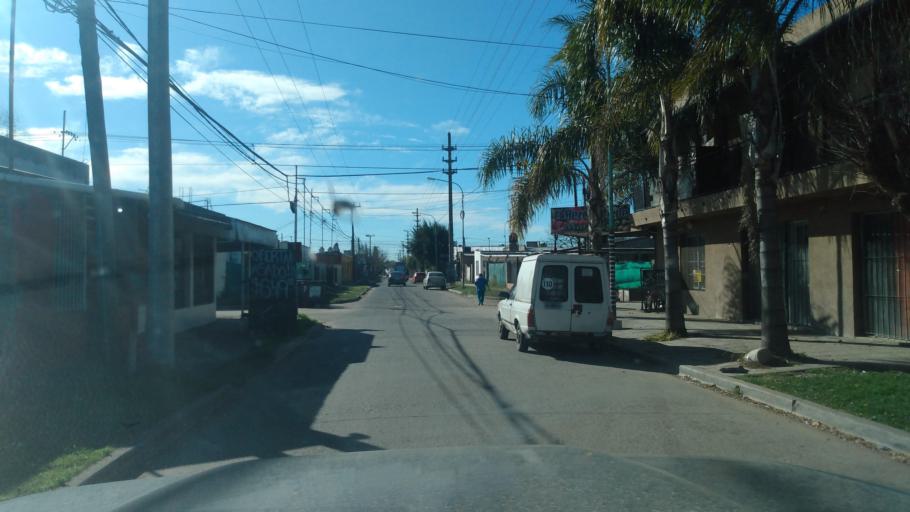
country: AR
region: Buenos Aires
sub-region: Partido de Lujan
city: Lujan
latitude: -34.5650
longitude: -59.0928
